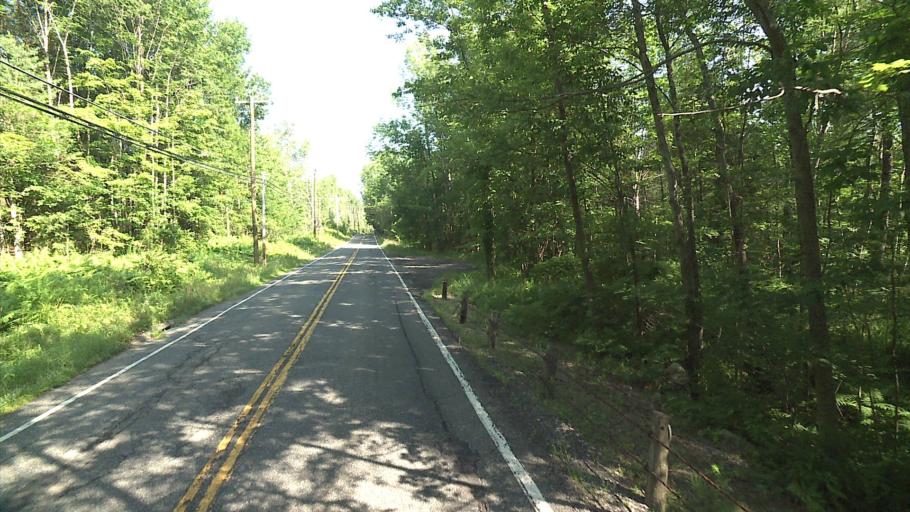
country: US
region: Connecticut
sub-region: Litchfield County
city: Winsted
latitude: 41.9985
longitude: -73.1015
